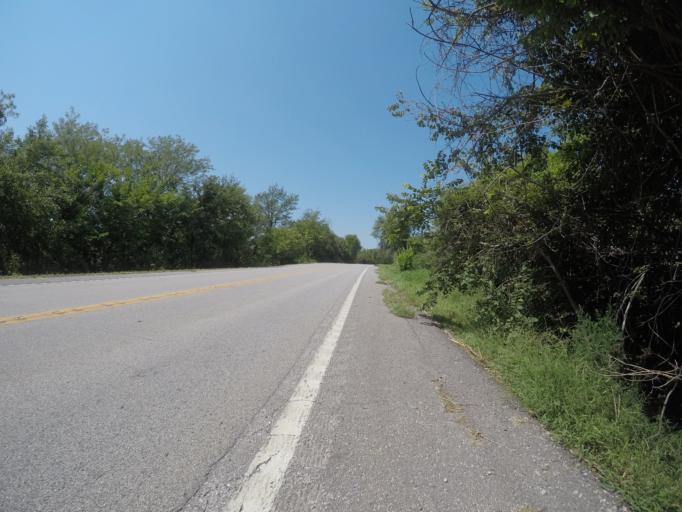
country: US
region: Missouri
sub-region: Platte County
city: Weston
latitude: 39.4352
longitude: -94.9194
